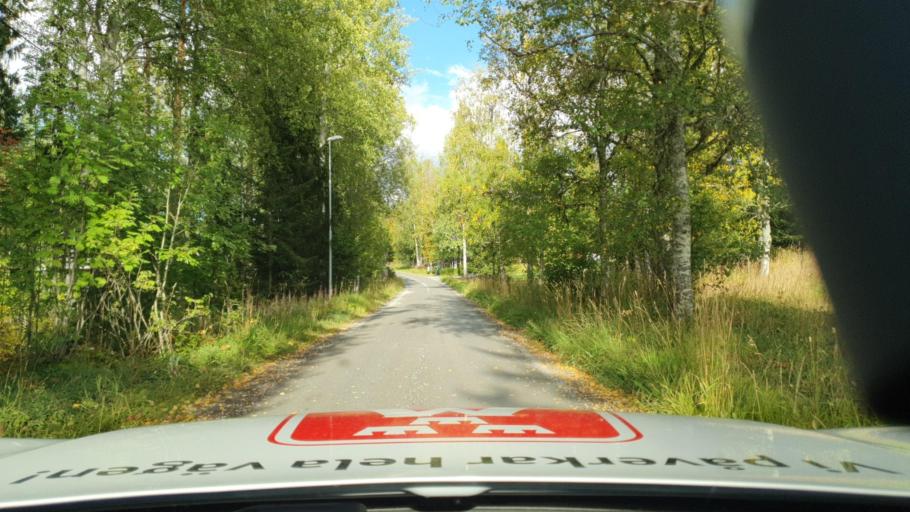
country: SE
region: Jaemtland
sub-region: OEstersunds Kommun
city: Brunflo
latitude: 63.1071
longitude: 14.8003
